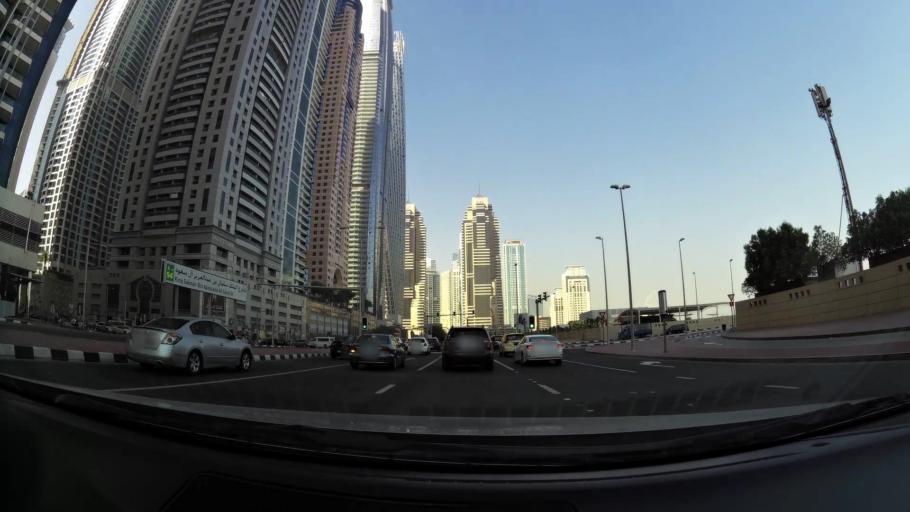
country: AE
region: Dubai
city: Dubai
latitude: 25.0902
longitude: 55.1470
